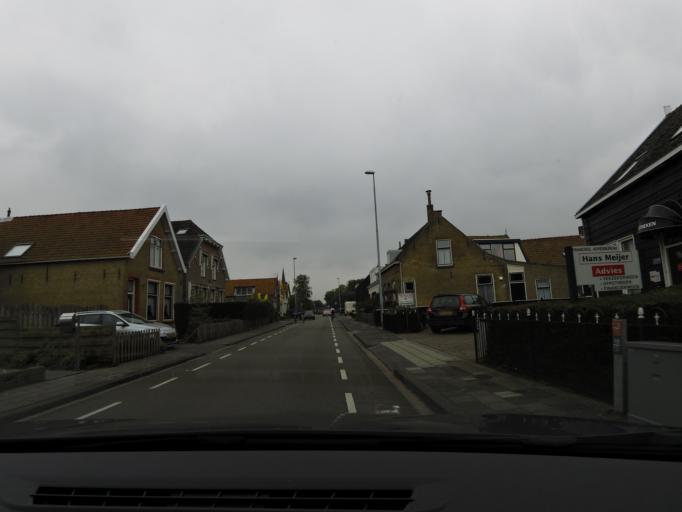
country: NL
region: South Holland
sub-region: Gemeente Goeree-Overflakkee
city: Middelharnis
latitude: 51.7596
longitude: 4.1552
